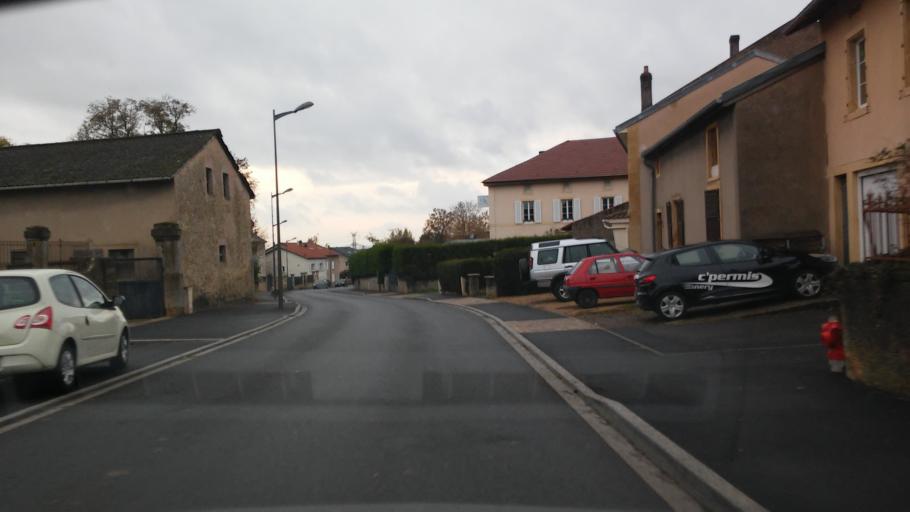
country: FR
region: Lorraine
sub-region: Departement de la Moselle
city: Vigy
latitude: 49.2041
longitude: 6.2947
